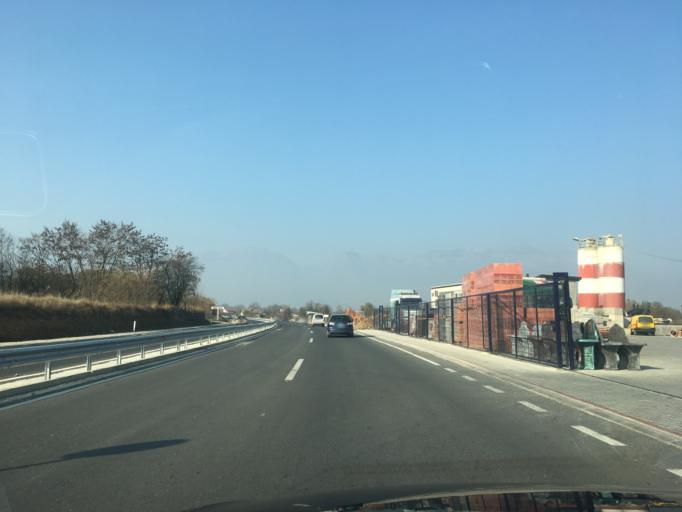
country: XK
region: Pec
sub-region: Komuna e Pejes
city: Dubova (Driloni)
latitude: 42.6576
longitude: 20.3856
